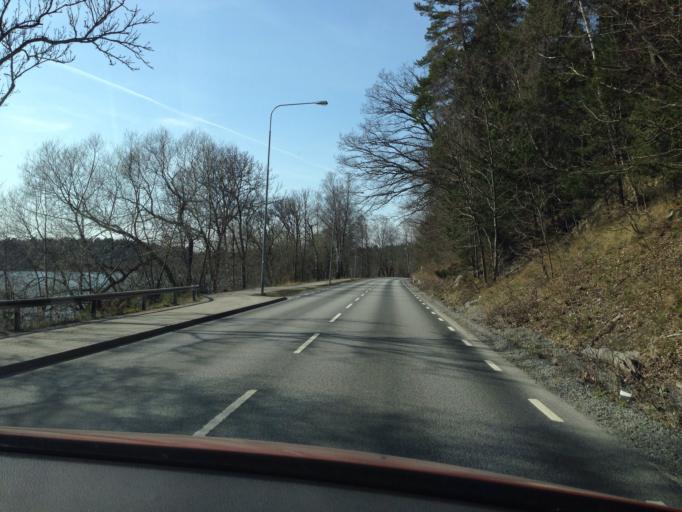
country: SE
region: Stockholm
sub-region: Botkyrka Kommun
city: Eriksberg
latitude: 59.2405
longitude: 17.7959
